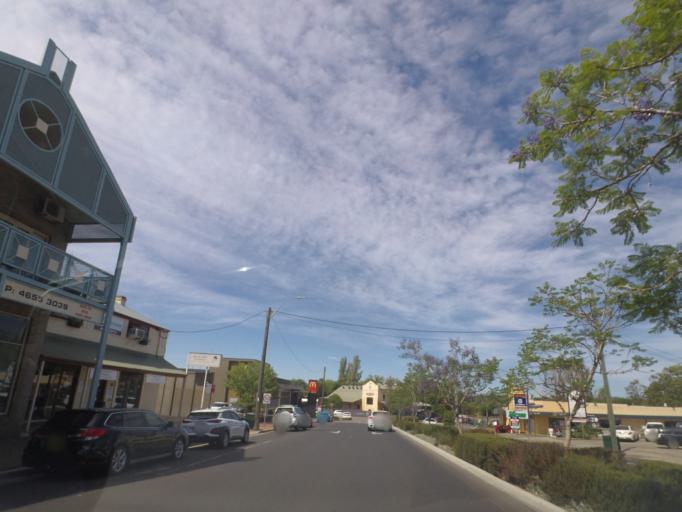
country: AU
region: New South Wales
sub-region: Camden
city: Elderslie
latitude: -34.0535
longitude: 150.6982
